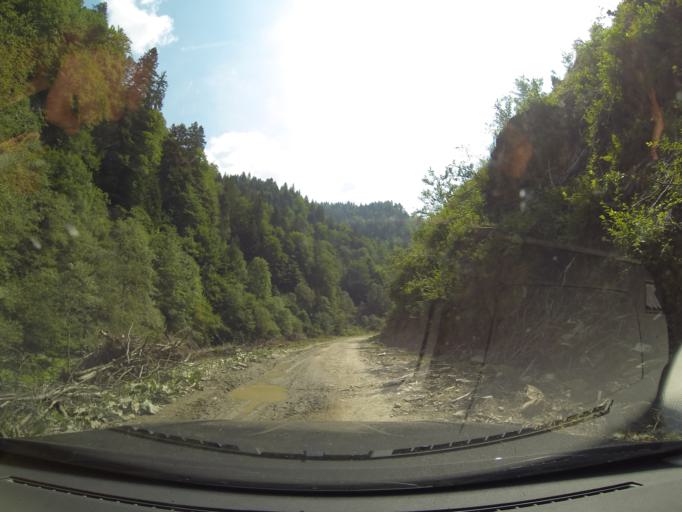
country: RO
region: Arges
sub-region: Comuna Arefu
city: Arefu
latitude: 45.4849
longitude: 24.6374
